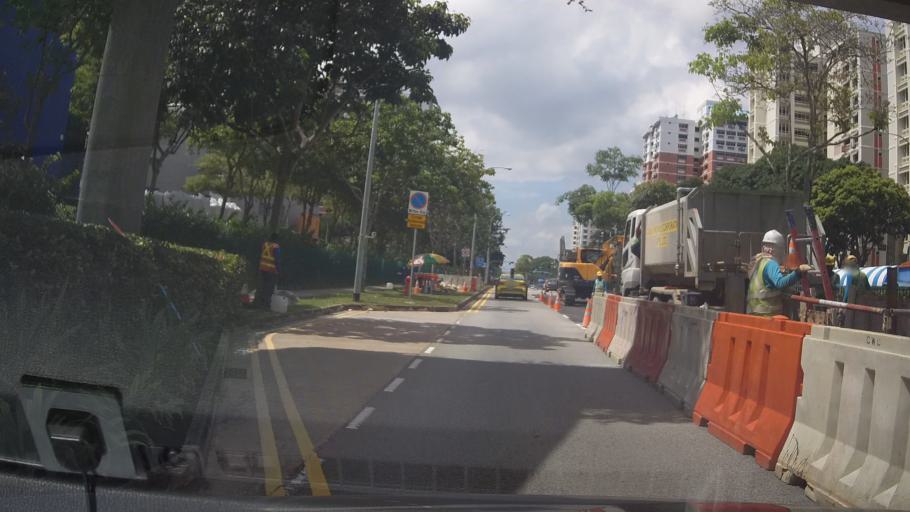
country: MY
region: Johor
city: Kampung Pasir Gudang Baru
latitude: 1.3769
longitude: 103.9382
